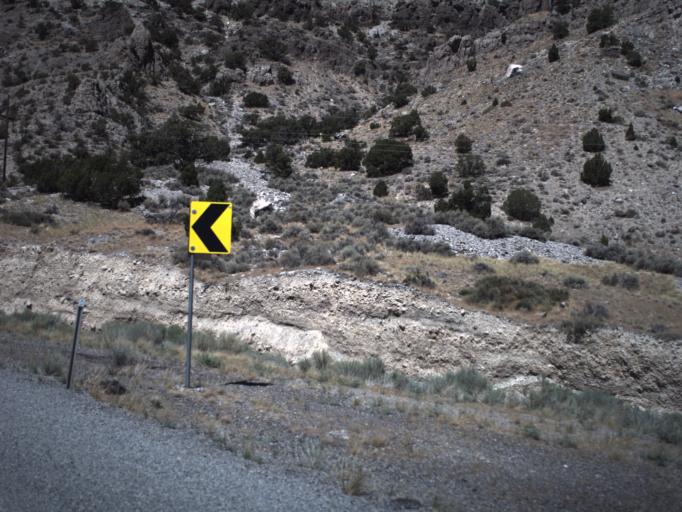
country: US
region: Utah
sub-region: Beaver County
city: Milford
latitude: 39.0873
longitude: -113.5673
